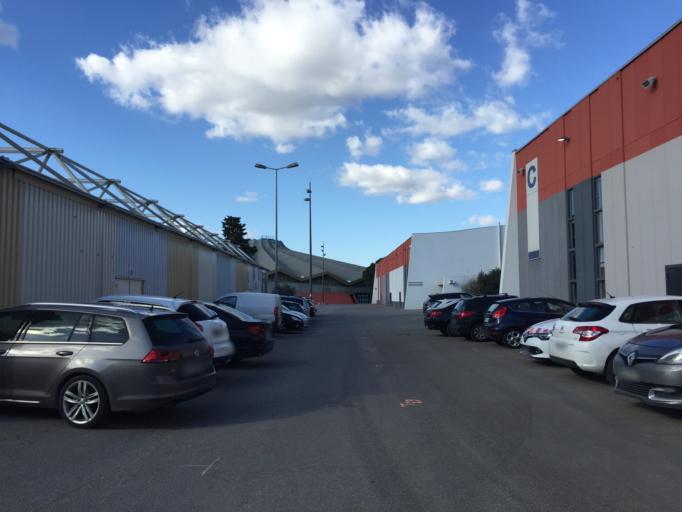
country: FR
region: Provence-Alpes-Cote d'Azur
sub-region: Departement des Bouches-du-Rhone
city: Noves
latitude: 43.9061
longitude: 4.8931
